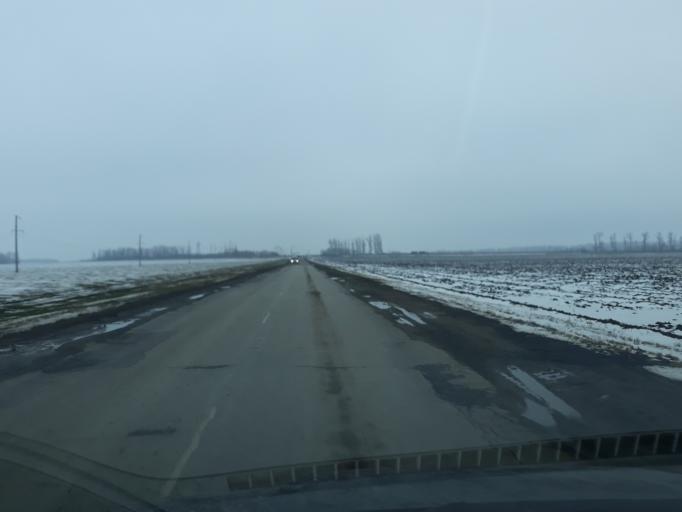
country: RU
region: Rostov
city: Severnyy
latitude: 47.3648
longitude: 39.6349
